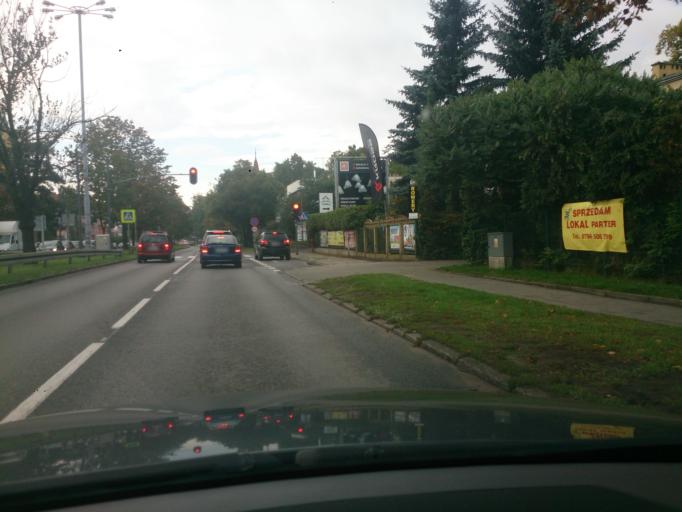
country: PL
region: Pomeranian Voivodeship
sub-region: Sopot
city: Sopot
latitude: 54.4277
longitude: 18.5625
